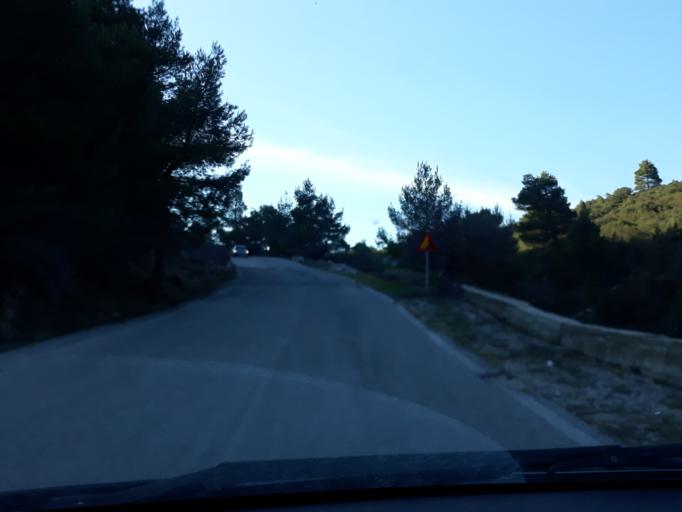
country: GR
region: Attica
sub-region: Nomarchia Dytikis Attikis
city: Fyli
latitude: 38.1568
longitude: 23.6304
